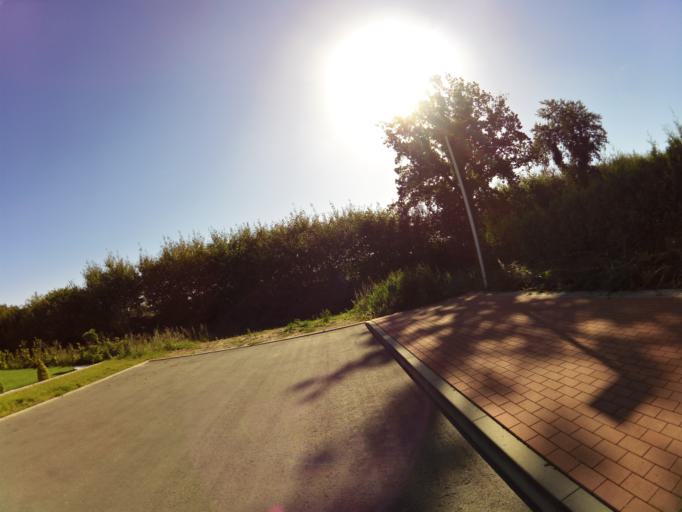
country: DE
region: Schleswig-Holstein
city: Windeby
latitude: 54.4565
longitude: 9.8217
